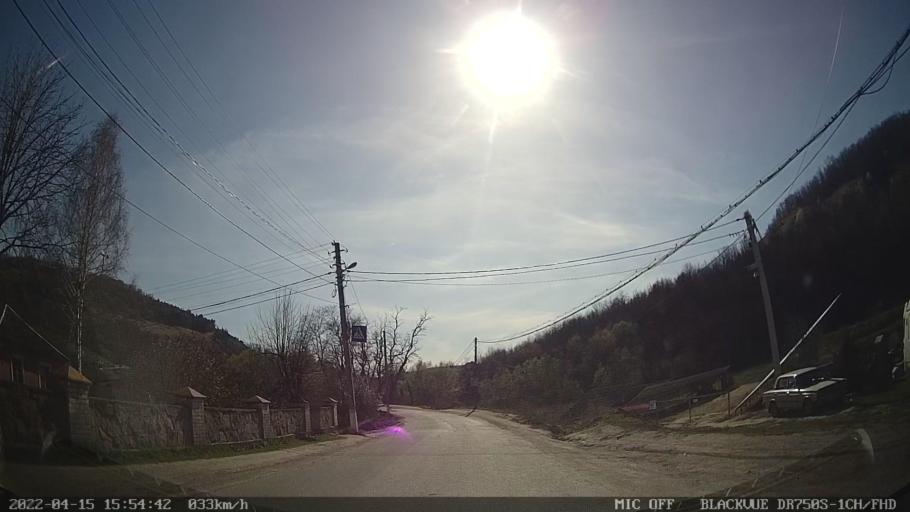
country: MD
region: Raionul Ocnita
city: Otaci
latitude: 48.4029
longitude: 27.8886
